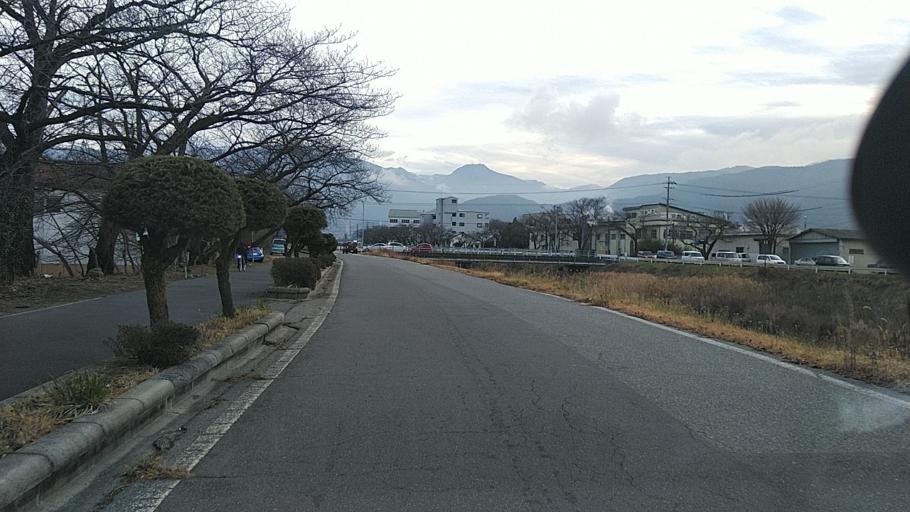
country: JP
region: Nagano
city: Matsumoto
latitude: 36.2258
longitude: 137.9748
